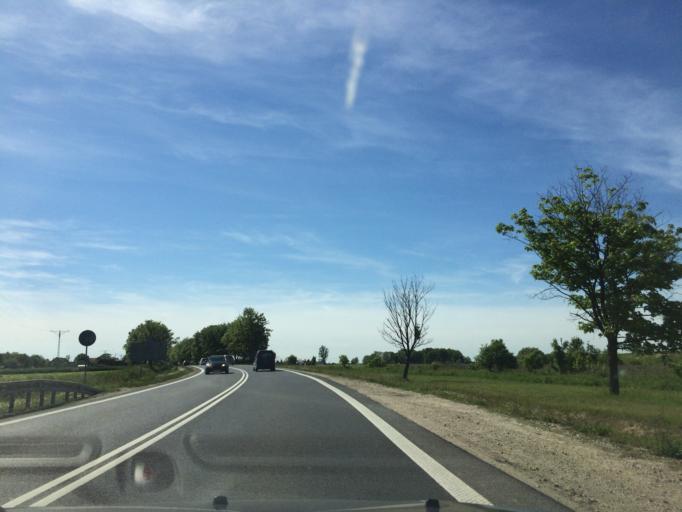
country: PL
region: Lower Silesian Voivodeship
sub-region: Powiat wroclawski
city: Tyniec Maly
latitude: 51.0124
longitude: 16.8831
